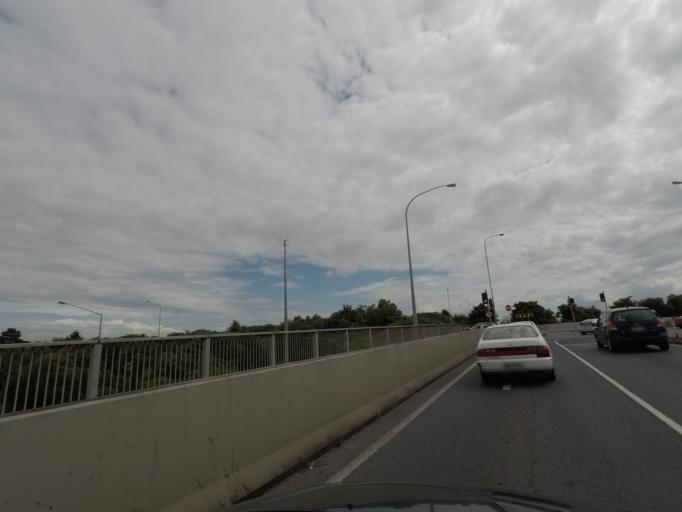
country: NZ
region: Auckland
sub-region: Auckland
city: Manukau City
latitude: -36.9522
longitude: 174.8590
